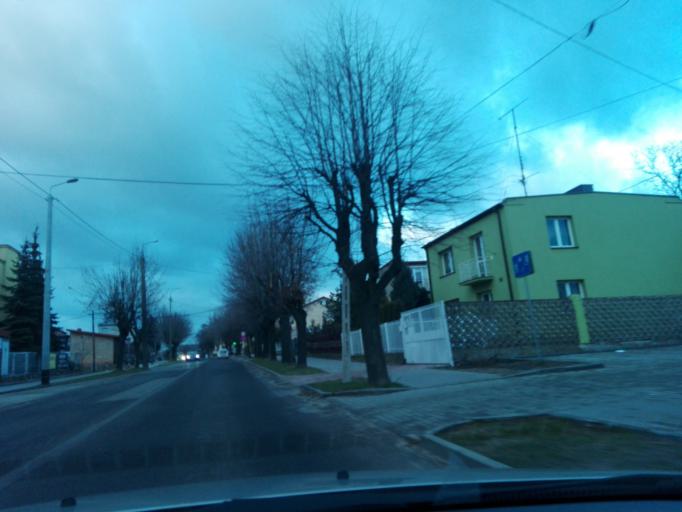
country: PL
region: Lodz Voivodeship
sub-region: Powiat kutnowski
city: Kutno
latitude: 52.2387
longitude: 19.3530
